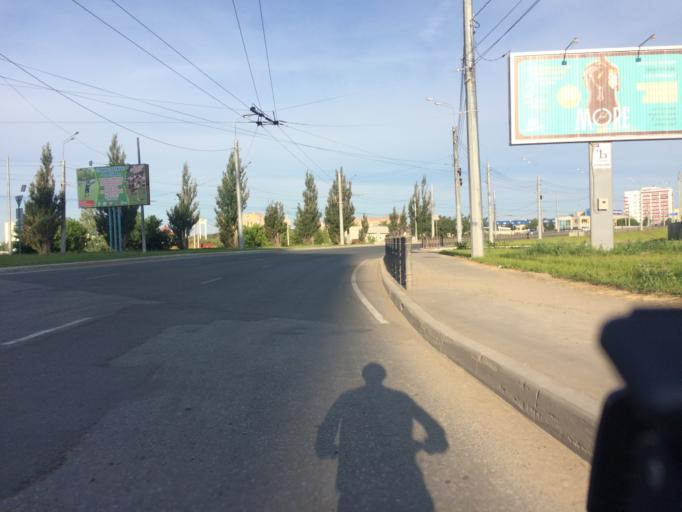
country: RU
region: Mariy-El
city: Yoshkar-Ola
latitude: 56.6280
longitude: 47.9035
